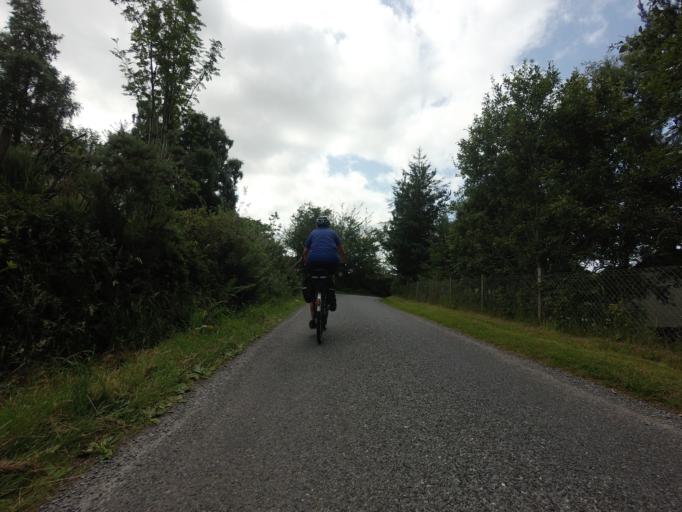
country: GB
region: Scotland
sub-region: Highland
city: Fortrose
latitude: 57.4740
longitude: -4.0647
